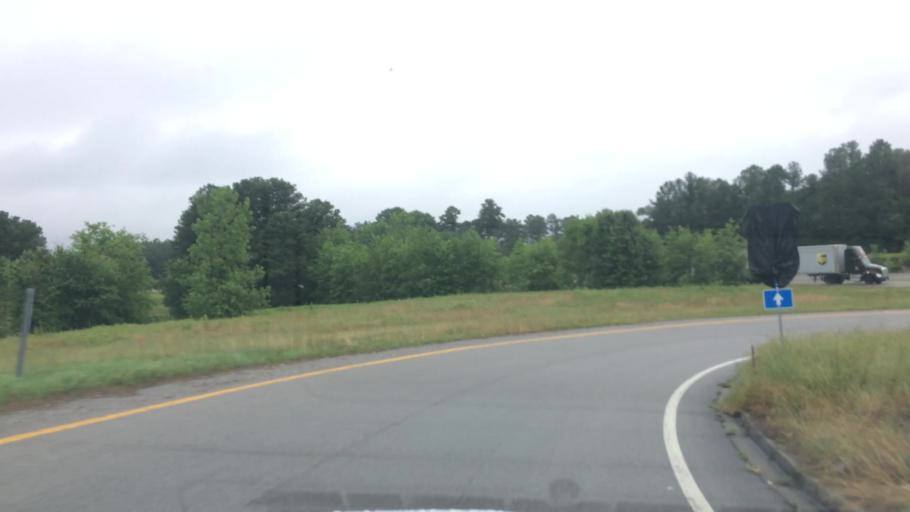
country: US
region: South Carolina
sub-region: Richland County
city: Dentsville
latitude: 34.0821
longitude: -80.9425
